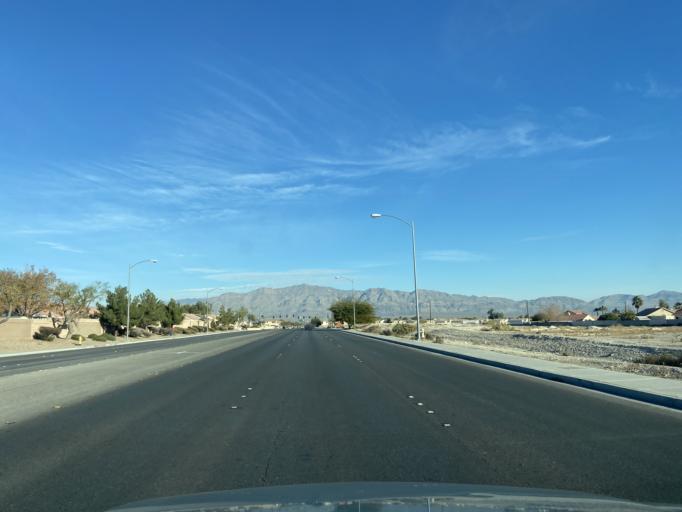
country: US
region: Nevada
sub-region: Clark County
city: North Las Vegas
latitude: 36.2442
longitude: -115.1800
